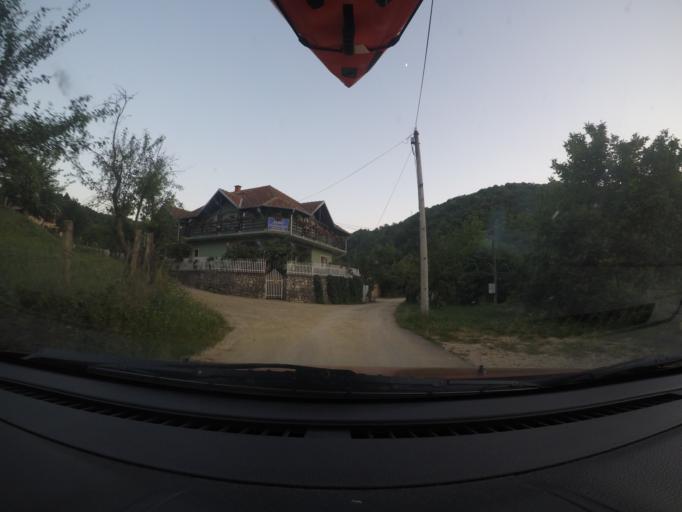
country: RO
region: Mehedinti
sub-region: Comuna Svinita
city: Svinita
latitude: 44.4633
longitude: 22.1381
